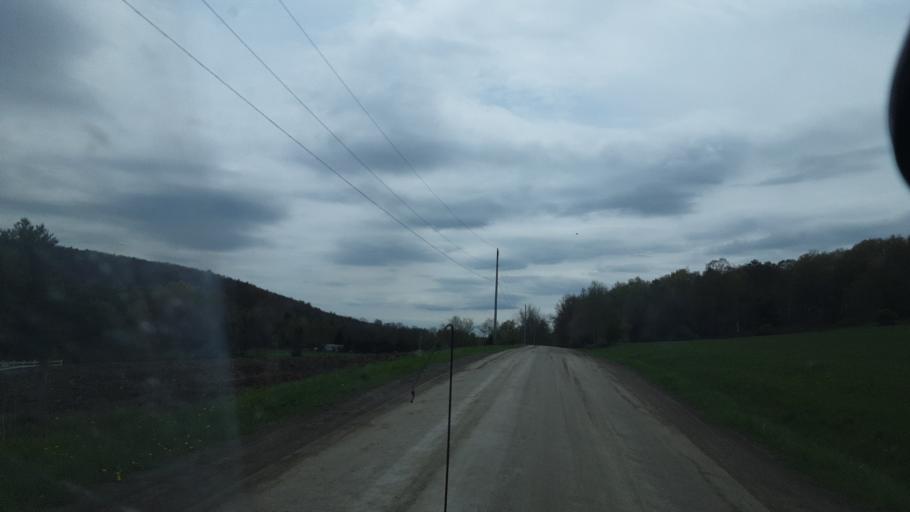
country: US
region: New York
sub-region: Steuben County
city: Addison
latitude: 42.1046
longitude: -77.3409
